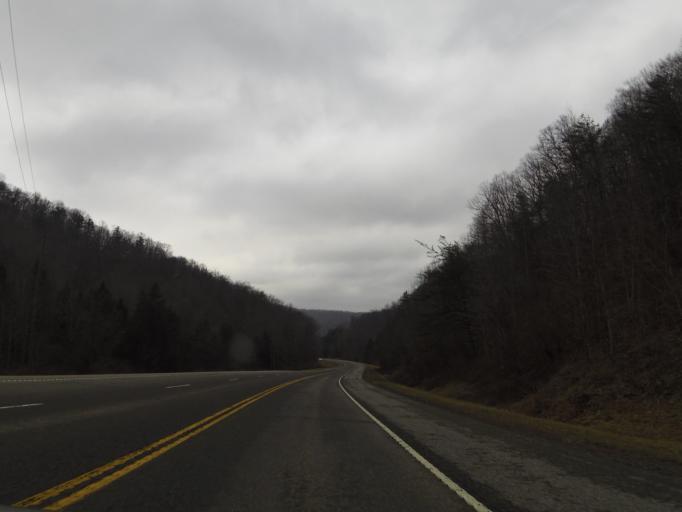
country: US
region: Tennessee
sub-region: Campbell County
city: Caryville
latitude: 36.4019
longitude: -84.3095
